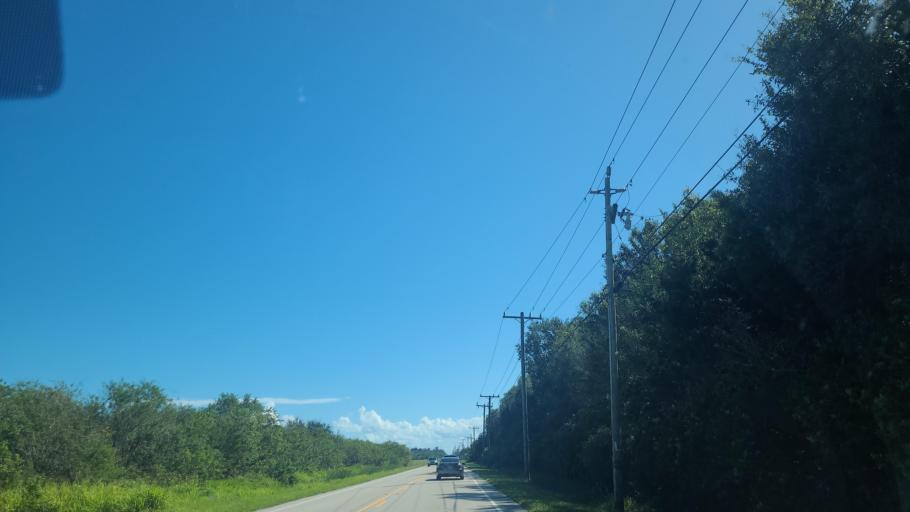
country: US
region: Florida
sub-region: Indian River County
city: Winter Beach
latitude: 27.7489
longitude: -80.4807
